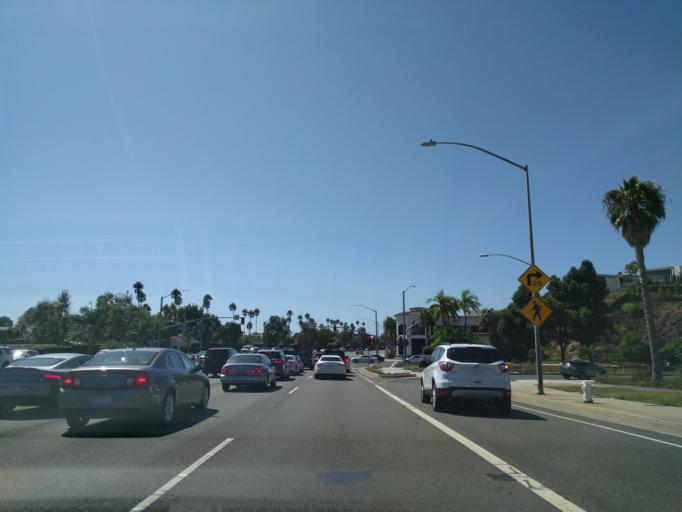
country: US
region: California
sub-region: Orange County
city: Newport Beach
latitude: 33.6166
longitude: -117.9062
